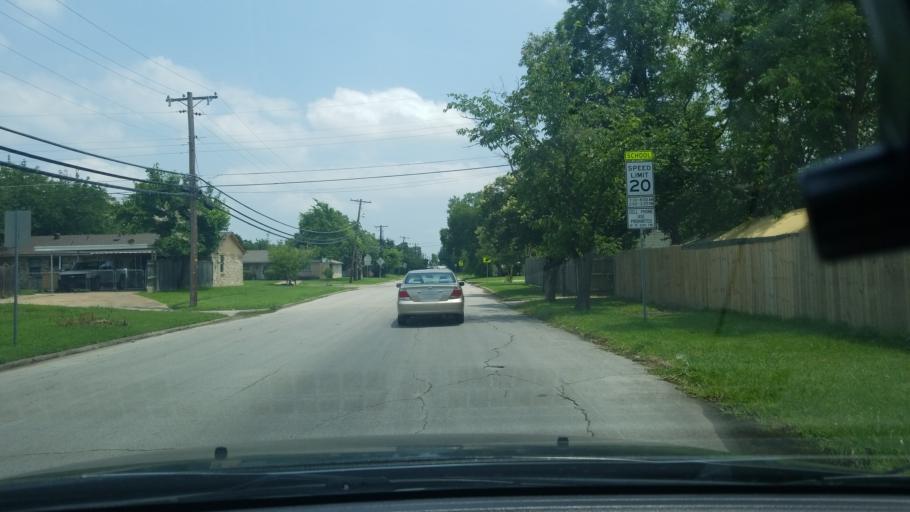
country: US
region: Texas
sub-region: Dallas County
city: Mesquite
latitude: 32.7968
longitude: -96.6426
